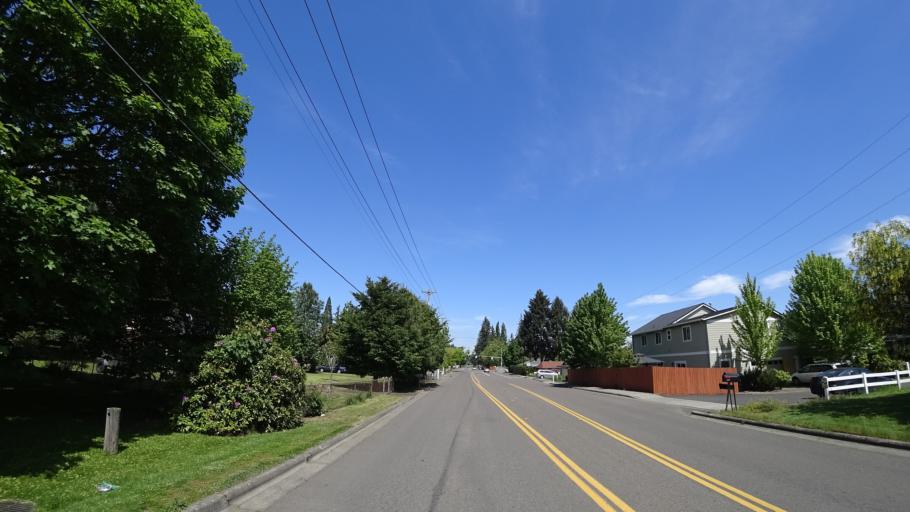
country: US
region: Oregon
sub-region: Washington County
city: Aloha
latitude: 45.4825
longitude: -122.8420
